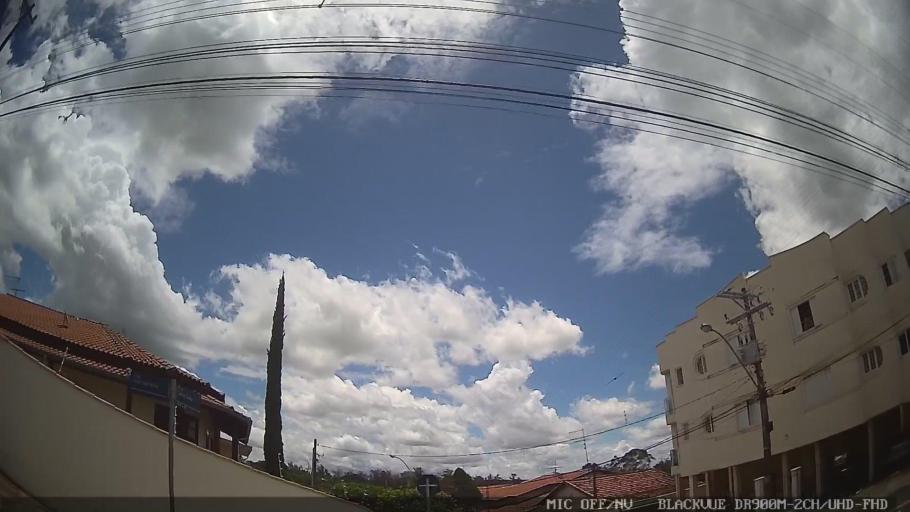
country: BR
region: Sao Paulo
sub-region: Jaguariuna
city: Jaguariuna
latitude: -22.7130
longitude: -46.9808
